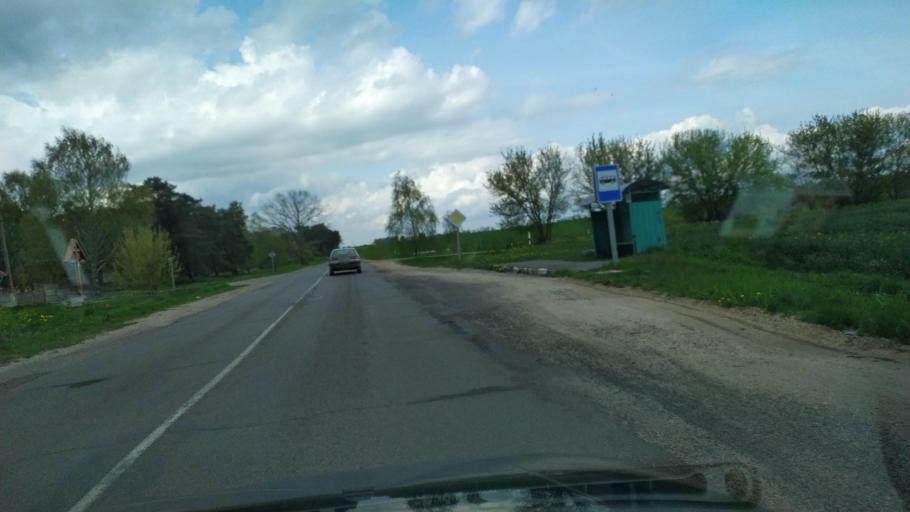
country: BY
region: Brest
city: Pruzhany
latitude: 52.5977
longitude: 24.4046
